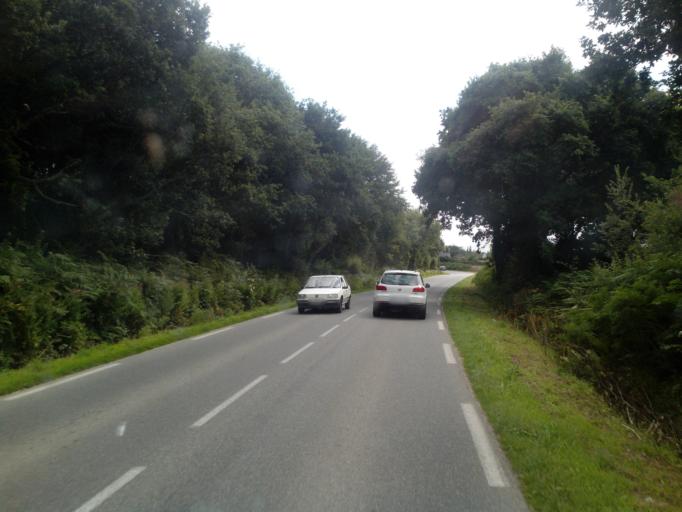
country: FR
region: Brittany
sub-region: Departement des Cotes-d'Armor
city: Plouha
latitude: 48.7025
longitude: -2.9488
